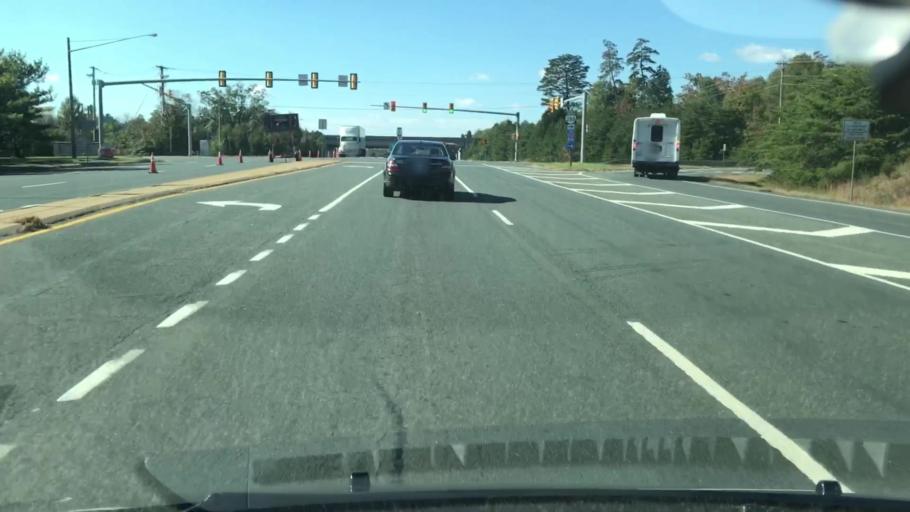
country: US
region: Virginia
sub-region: Fairfax County
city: Fairfax Station
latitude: 38.8295
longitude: -77.3635
